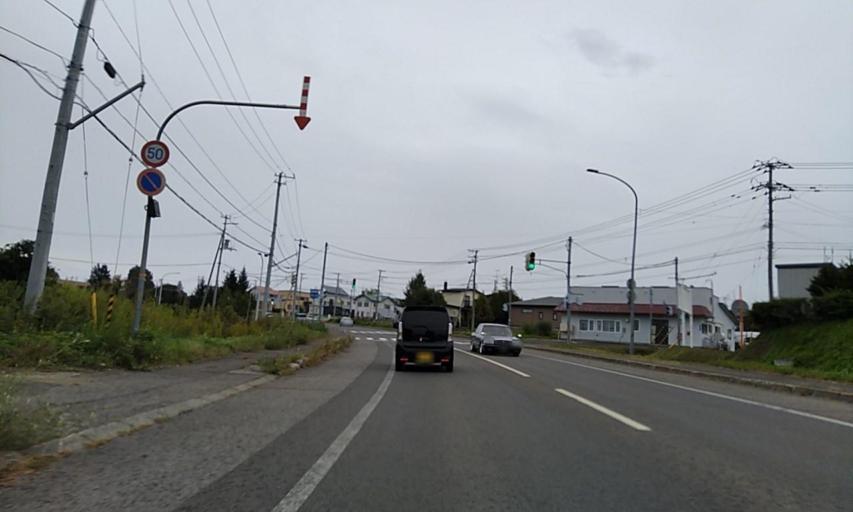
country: JP
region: Hokkaido
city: Bihoro
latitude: 43.9123
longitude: 144.1818
